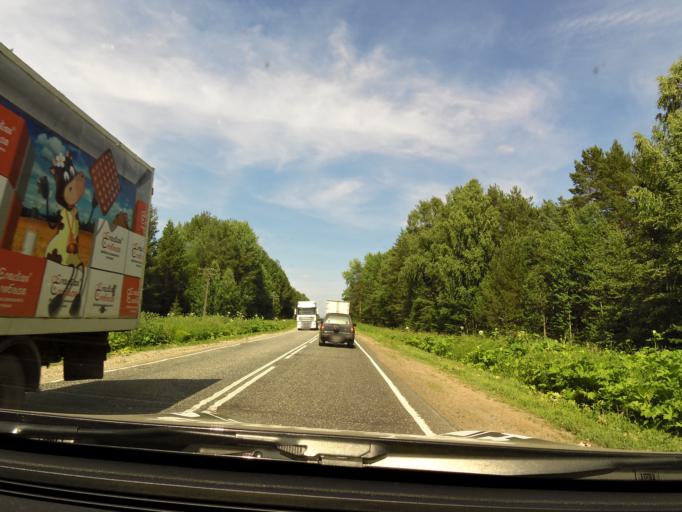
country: RU
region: Kirov
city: Slobodskoy
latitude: 58.7886
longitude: 50.5117
